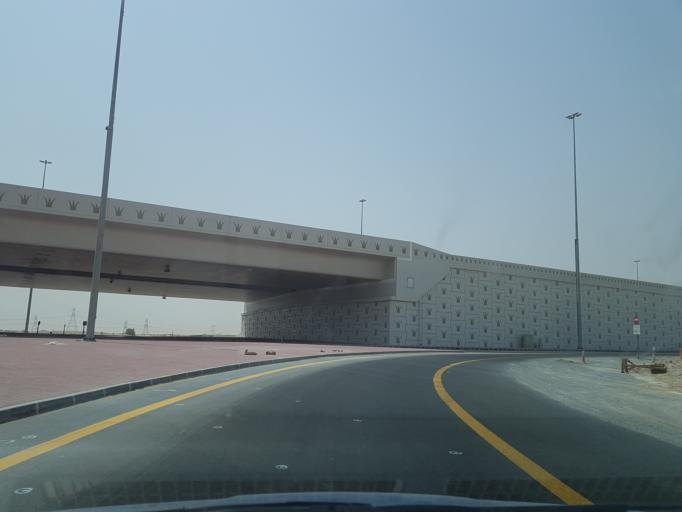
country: AE
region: Dubai
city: Dubai
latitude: 25.0586
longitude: 55.3006
